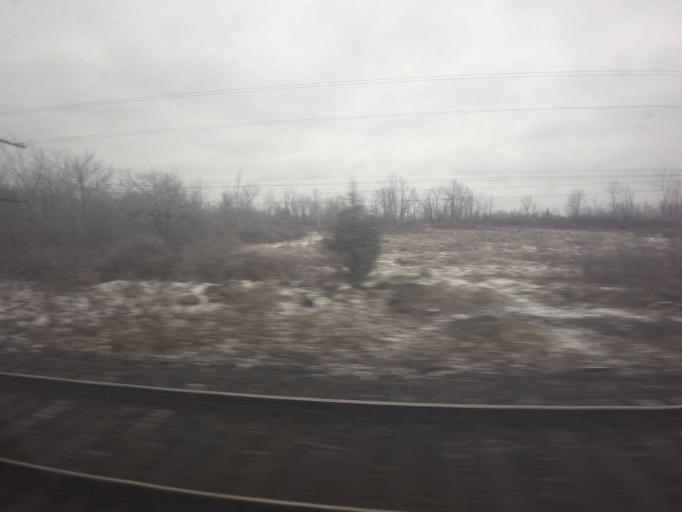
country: CA
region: Ontario
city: Gananoque
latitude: 44.3588
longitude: -76.2076
